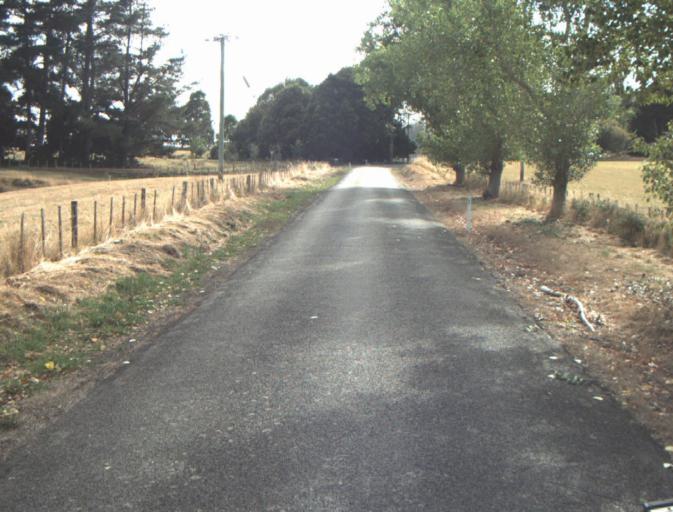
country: AU
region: Tasmania
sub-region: Launceston
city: Mayfield
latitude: -41.2868
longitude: 147.2130
